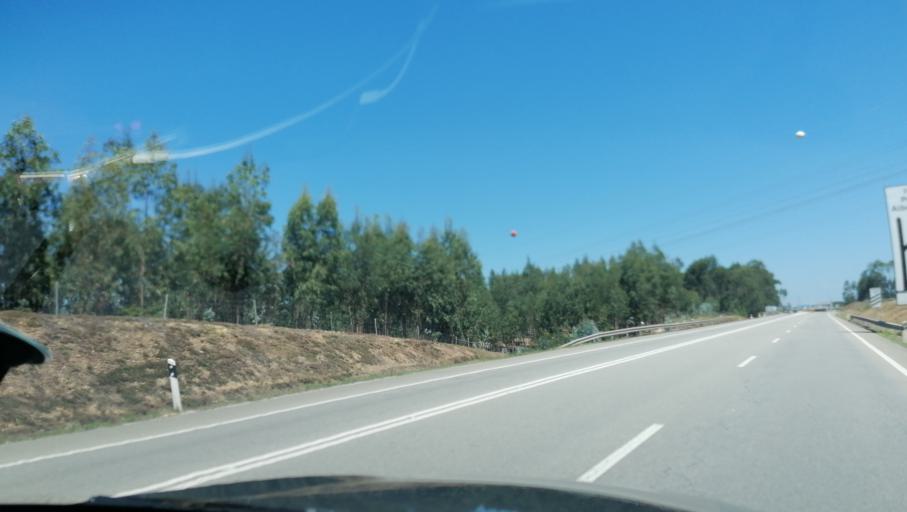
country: PT
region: Aveiro
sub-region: Agueda
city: Agueda
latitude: 40.5867
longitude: -8.4714
